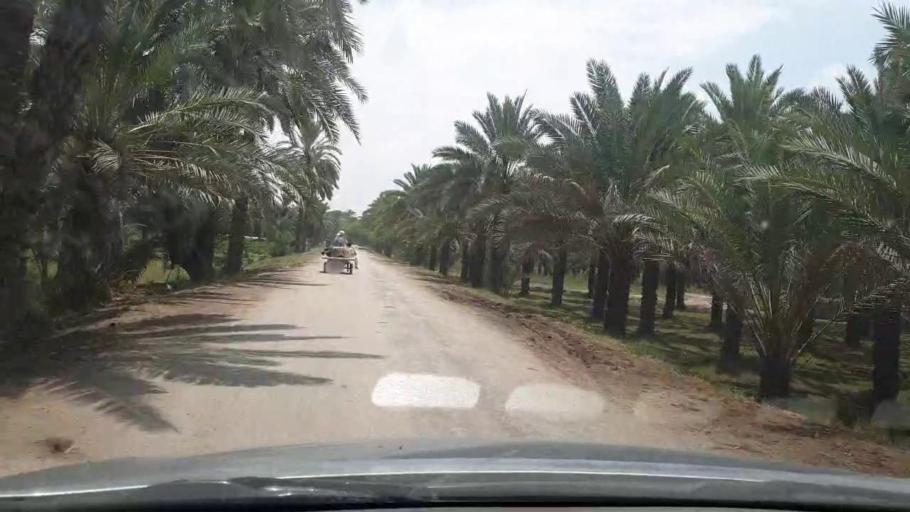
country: PK
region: Sindh
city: Khairpur
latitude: 27.4347
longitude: 68.7670
